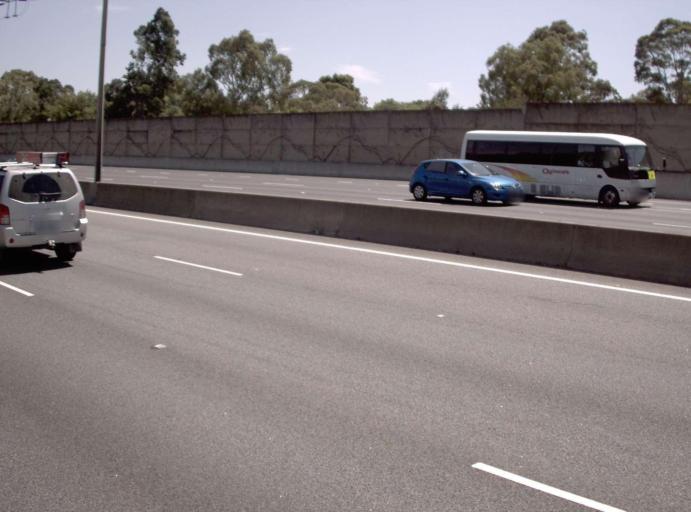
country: AU
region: Victoria
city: Glenferrie
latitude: -37.8386
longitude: 145.0378
